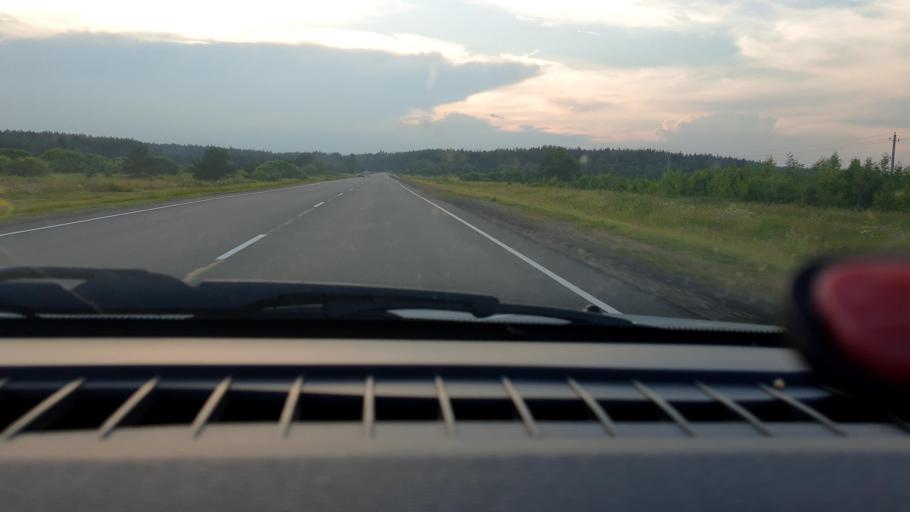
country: RU
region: Nizjnij Novgorod
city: Shatki
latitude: 55.1271
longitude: 44.2674
